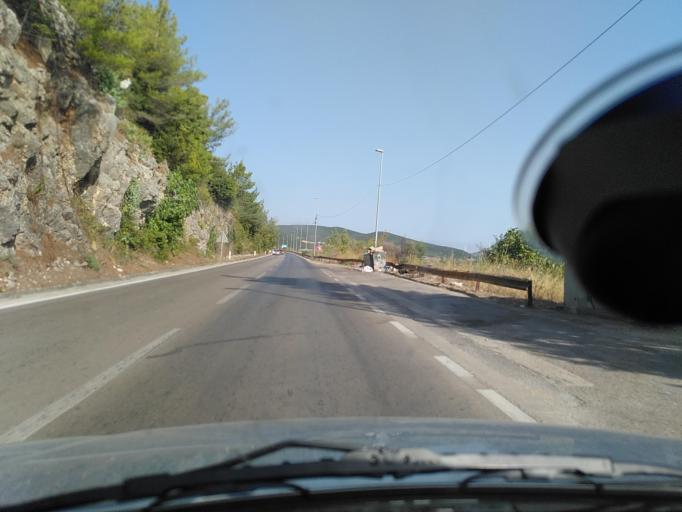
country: ME
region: Ulcinj
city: Ulcinj
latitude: 41.9441
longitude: 19.2084
